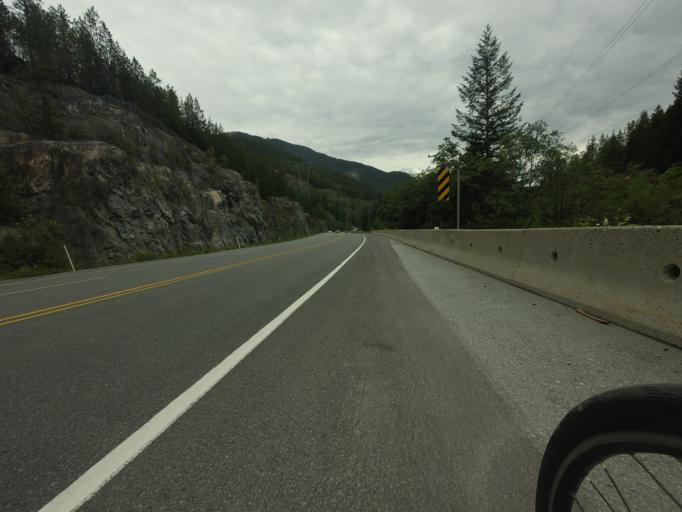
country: CA
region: British Columbia
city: Whistler
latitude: 49.8868
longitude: -123.1604
